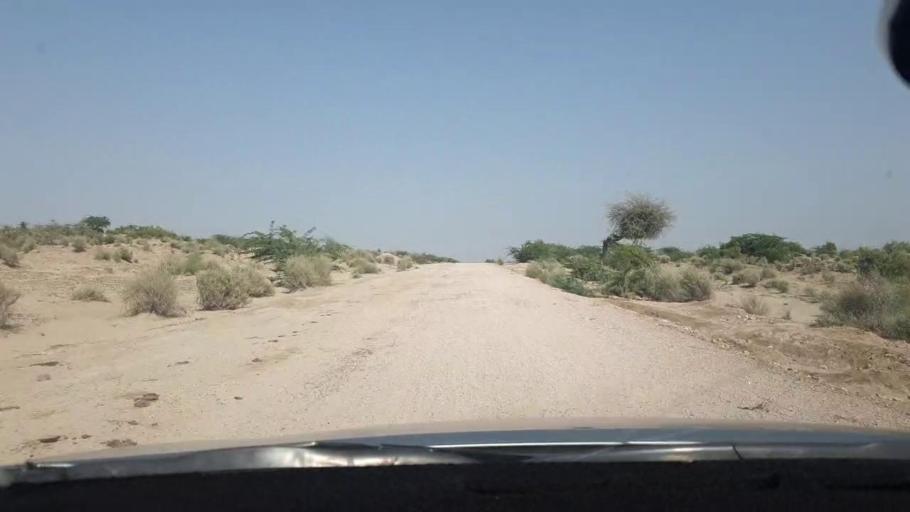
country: PK
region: Sindh
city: Pithoro
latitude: 25.7804
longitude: 69.4906
